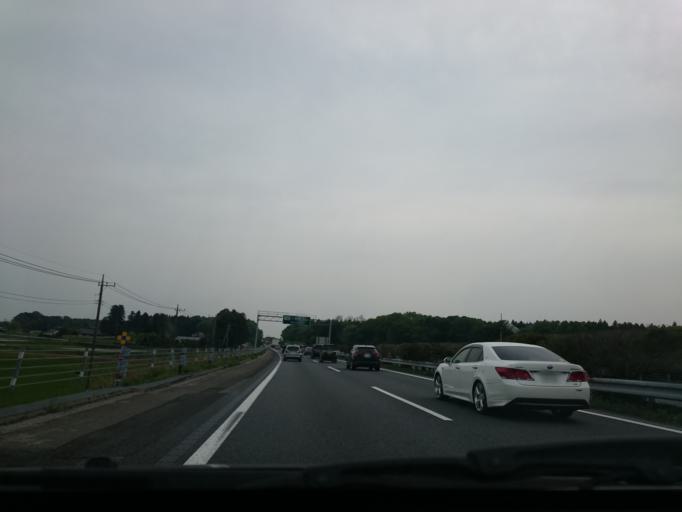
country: JP
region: Tochigi
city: Utsunomiya-shi
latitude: 36.6479
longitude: 139.8558
